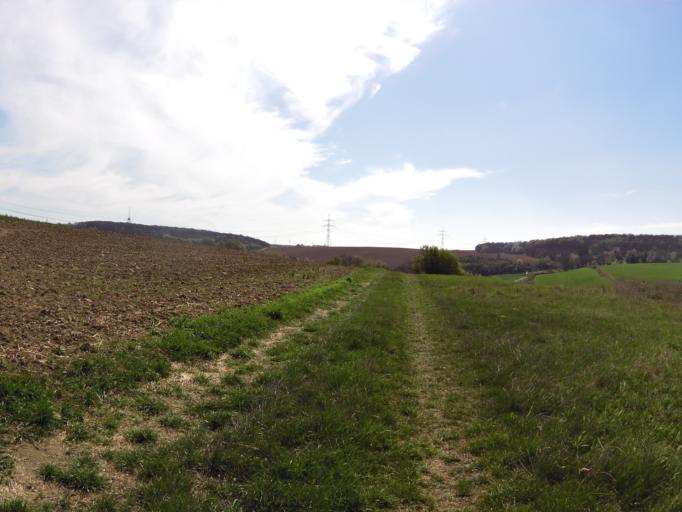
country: DE
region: Bavaria
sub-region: Regierungsbezirk Unterfranken
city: Rottendorf
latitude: 49.7858
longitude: 10.0384
